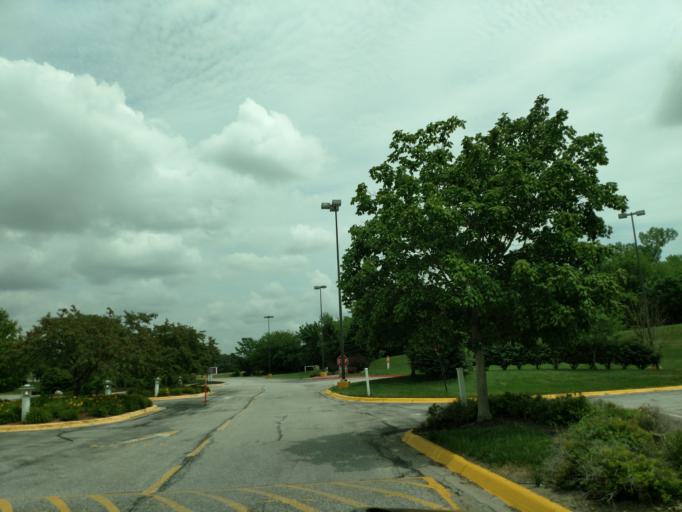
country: US
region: Nebraska
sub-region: Douglas County
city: Omaha
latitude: 41.2512
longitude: -95.9119
